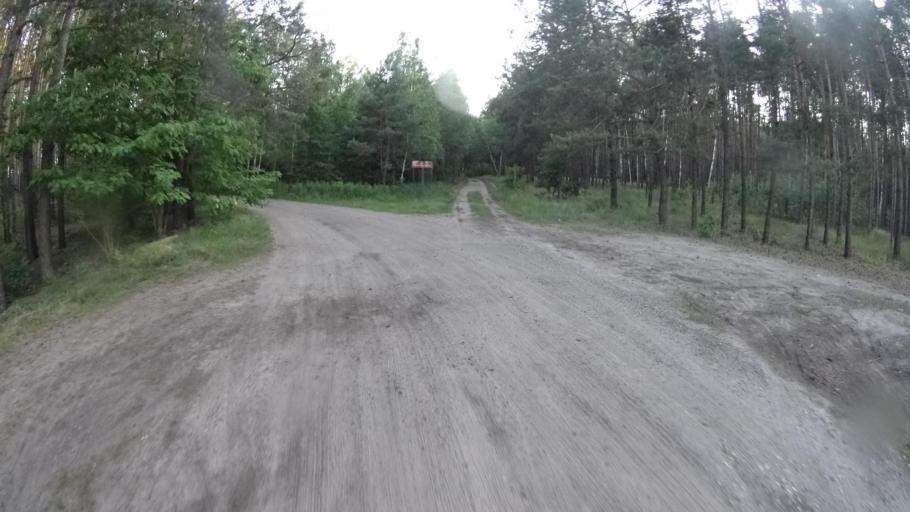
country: PL
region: Masovian Voivodeship
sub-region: Powiat warszawski zachodni
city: Jozefow
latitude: 52.2726
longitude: 20.6961
